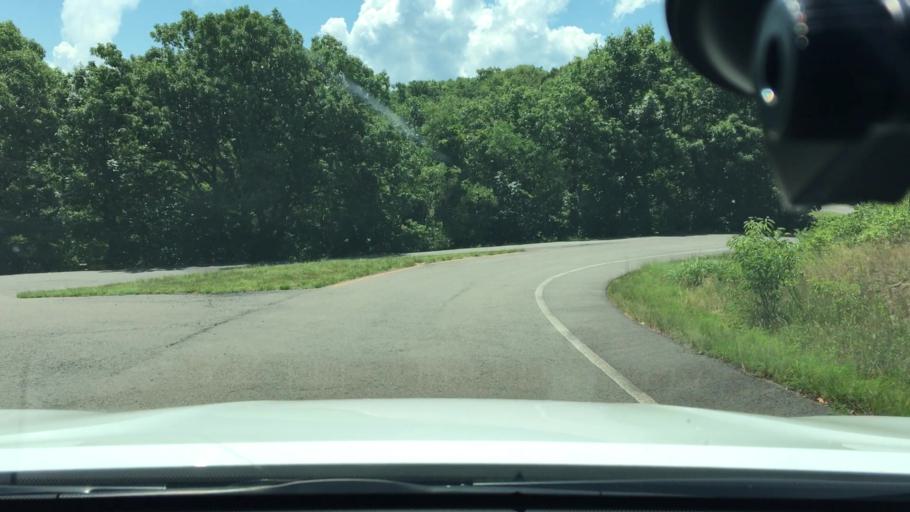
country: US
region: Arkansas
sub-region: Logan County
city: Paris
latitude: 35.1757
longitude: -93.6432
